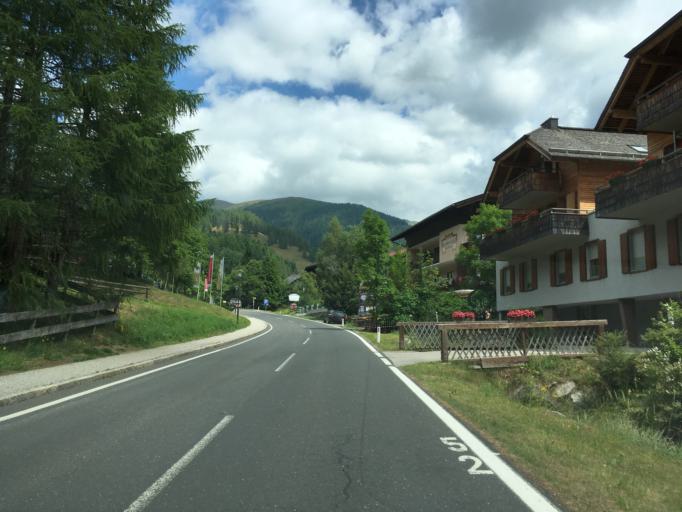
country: AT
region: Carinthia
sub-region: Politischer Bezirk Spittal an der Drau
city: Kleinkirchheim
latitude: 46.8406
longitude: 13.7658
